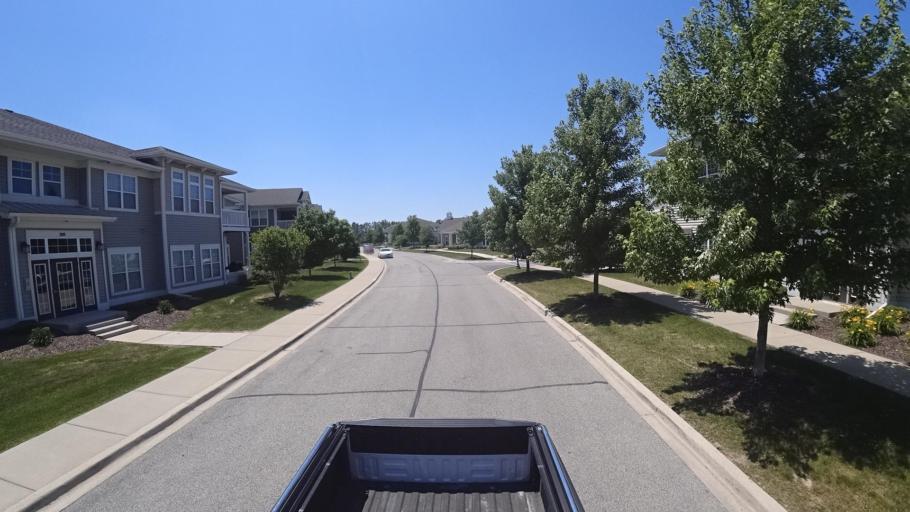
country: US
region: Indiana
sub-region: Porter County
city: Burns Harbor
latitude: 41.6056
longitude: -87.1310
